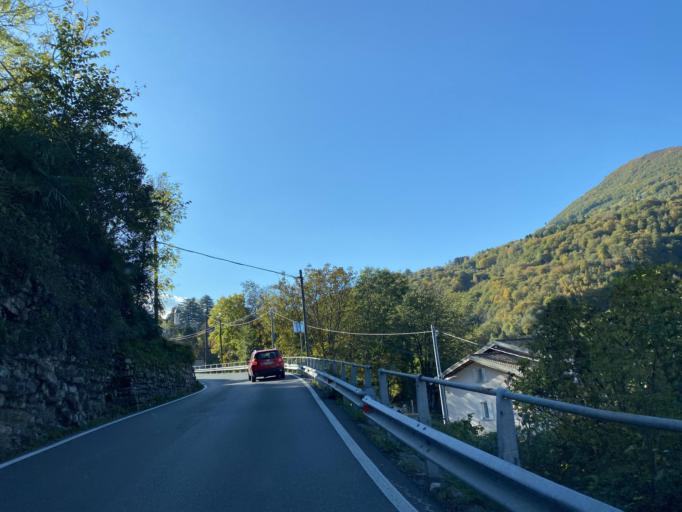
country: IT
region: Lombardy
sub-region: Provincia di Como
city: Osteno-Claino
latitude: 46.0049
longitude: 9.0871
